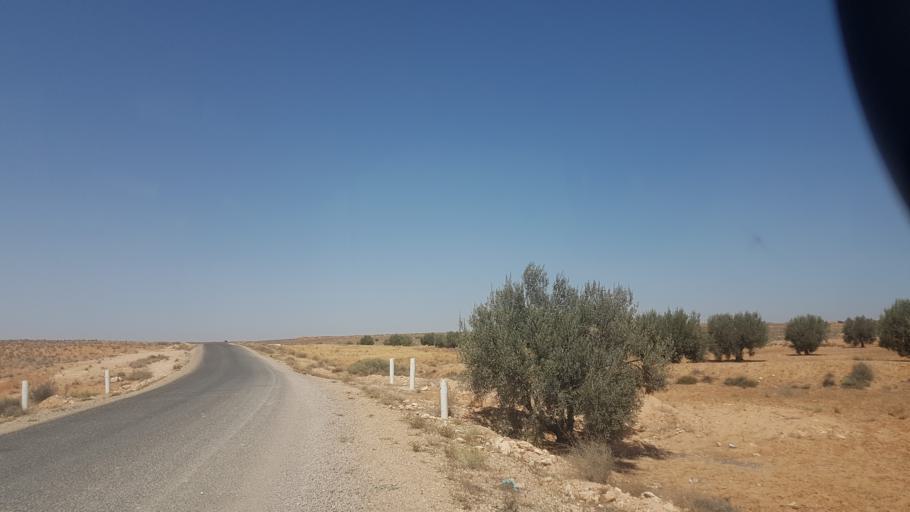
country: TN
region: Madanin
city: Medenine
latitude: 33.3189
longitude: 10.6031
